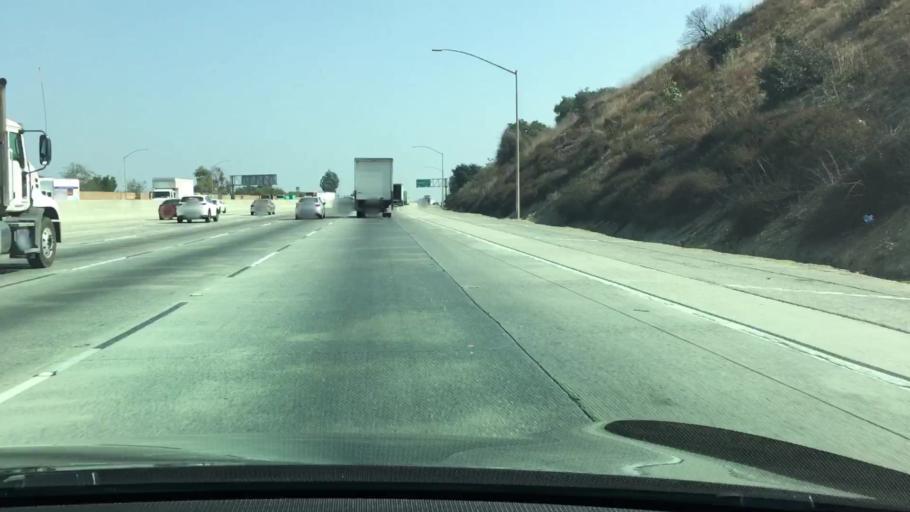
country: US
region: California
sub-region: Los Angeles County
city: Avocado Heights
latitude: 34.0289
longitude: -118.0076
